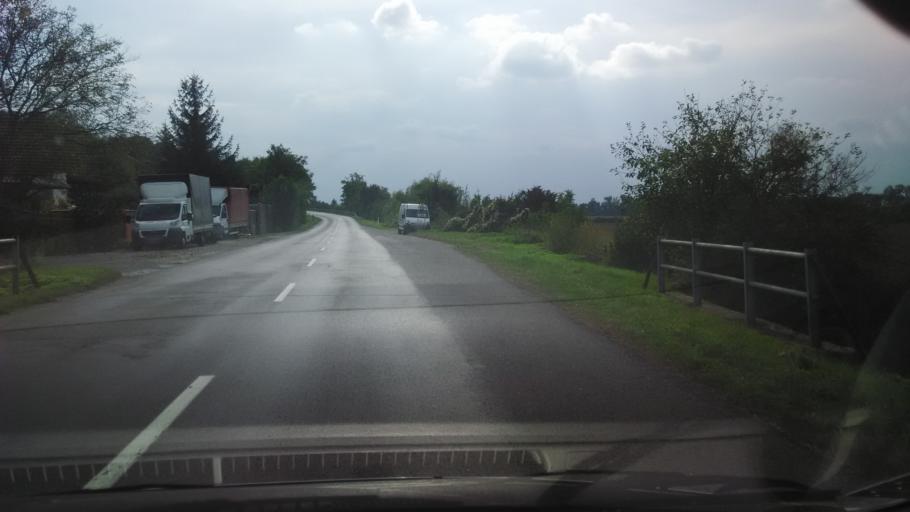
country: SK
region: Nitriansky
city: Levice
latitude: 48.1936
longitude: 18.6319
